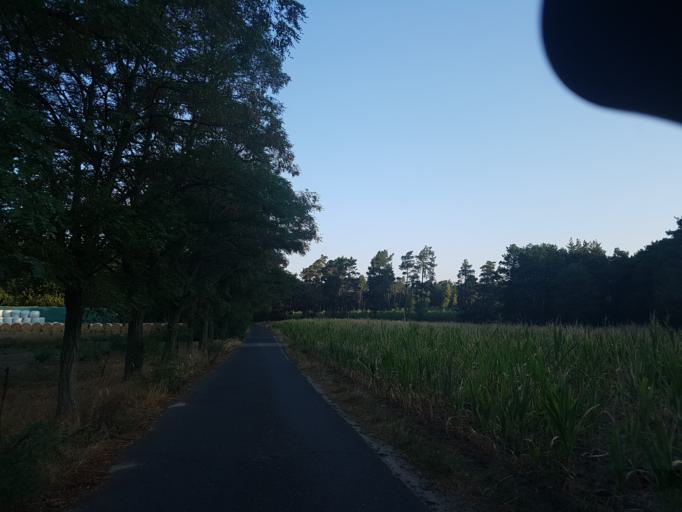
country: DE
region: Brandenburg
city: Falkenberg
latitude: 51.6481
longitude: 13.2878
